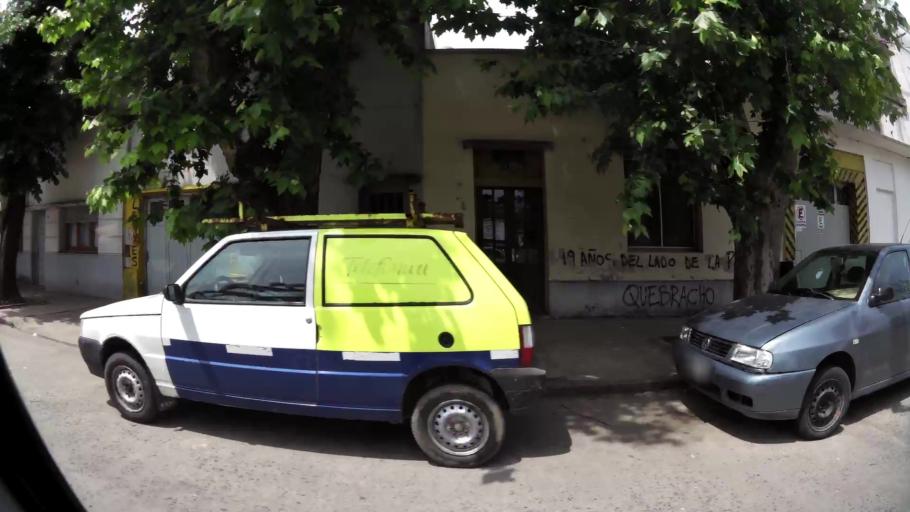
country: AR
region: Buenos Aires
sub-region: Partido de La Plata
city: La Plata
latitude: -34.9492
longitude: -57.9528
